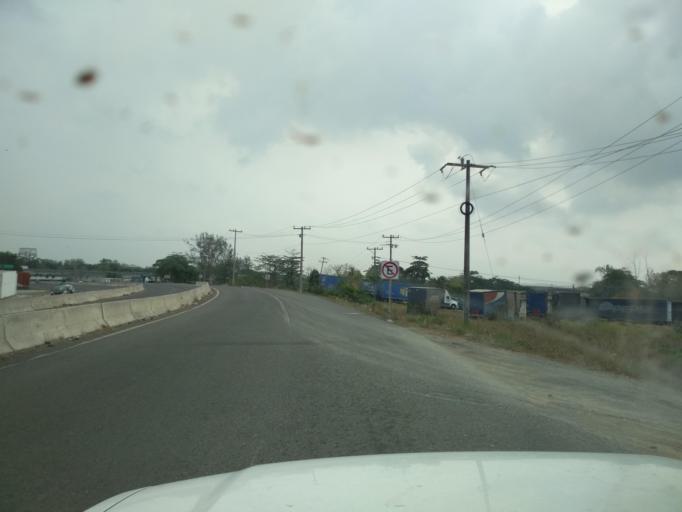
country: MX
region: Veracruz
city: Paso del Toro
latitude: 19.0197
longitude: -96.1354
